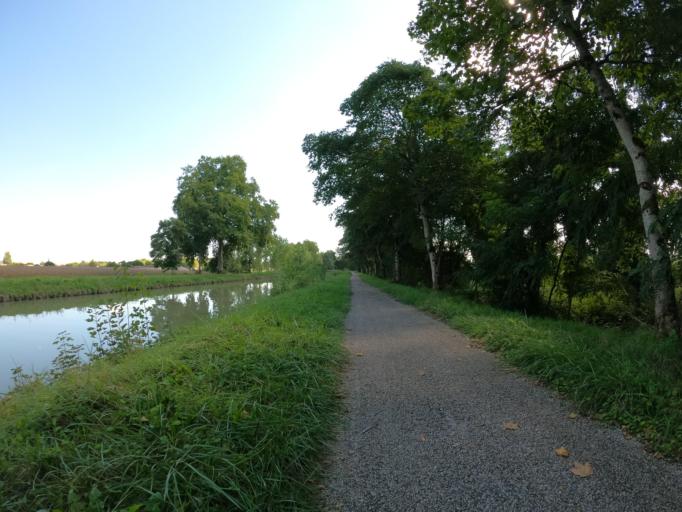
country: FR
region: Midi-Pyrenees
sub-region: Departement du Tarn-et-Garonne
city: Lamagistere
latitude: 44.1199
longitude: 0.8478
